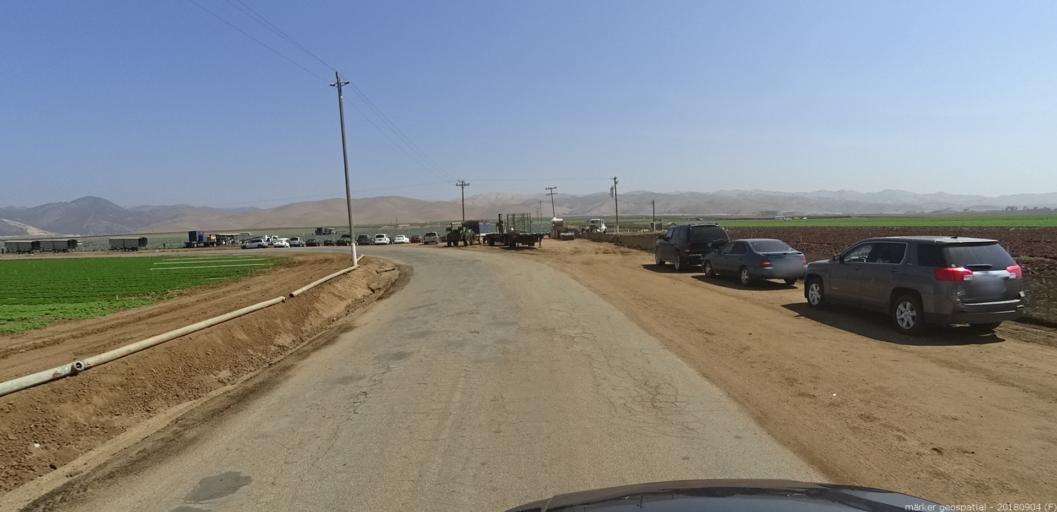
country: US
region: California
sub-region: Monterey County
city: Gonzales
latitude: 36.5383
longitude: -121.4264
